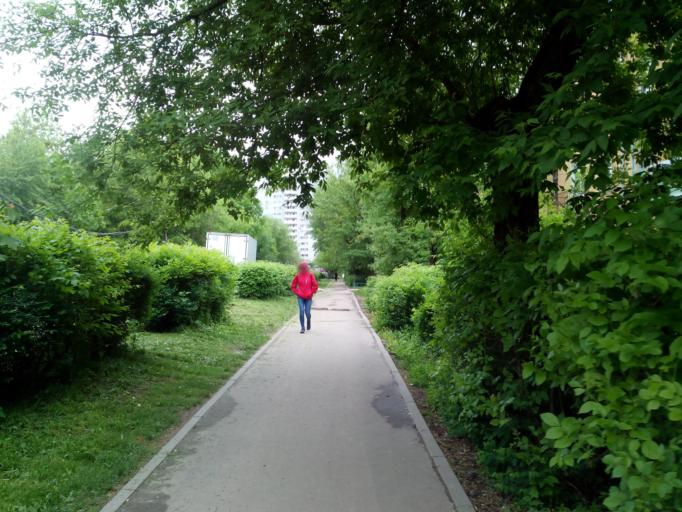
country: RU
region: Moskovskaya
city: Odintsovo
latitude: 55.6655
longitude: 37.2878
